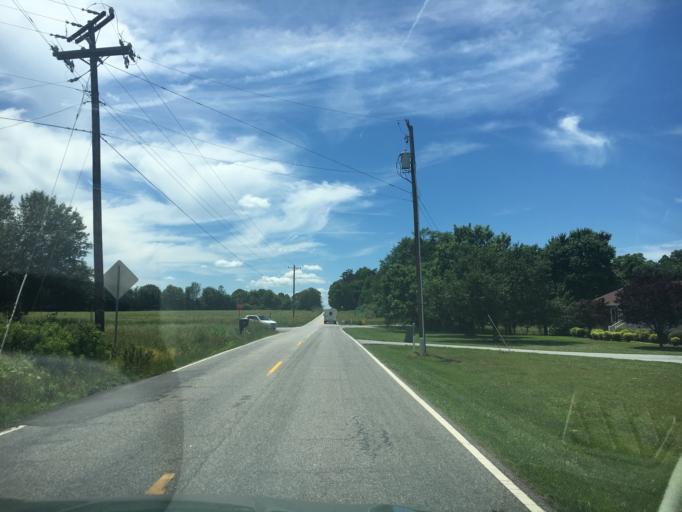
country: US
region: South Carolina
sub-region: Spartanburg County
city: Duncan
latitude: 34.8610
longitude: -82.1302
